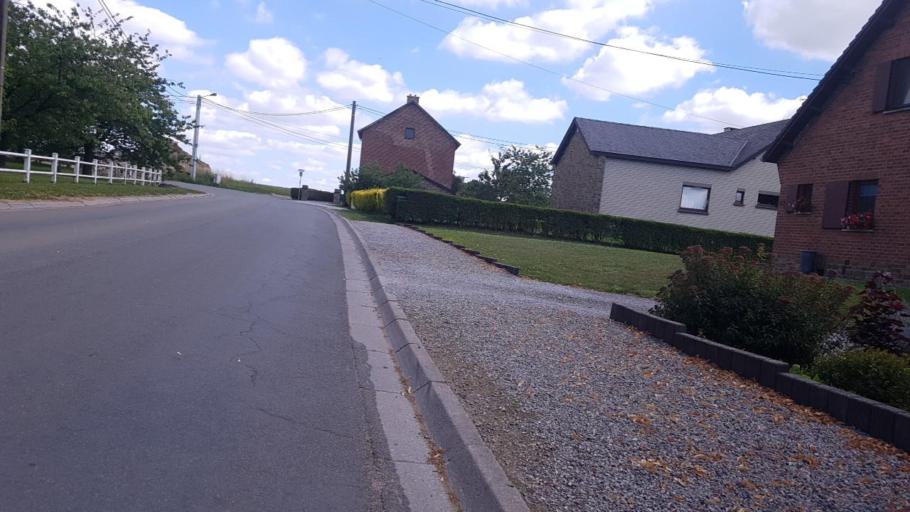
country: BE
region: Wallonia
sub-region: Province du Hainaut
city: Thuin
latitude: 50.3226
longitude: 4.3745
